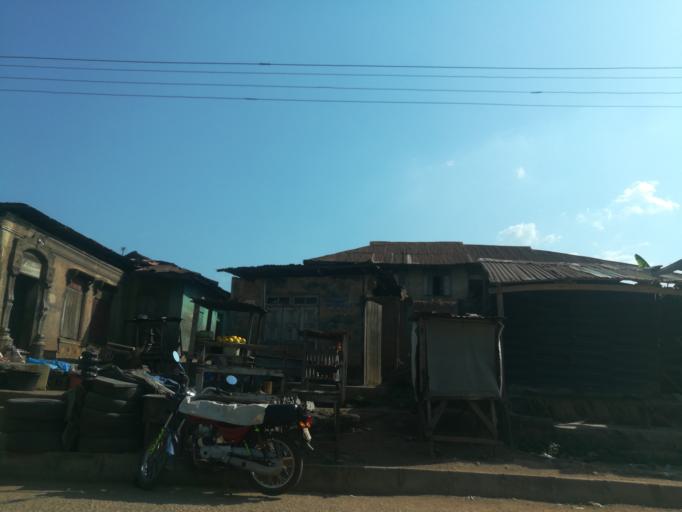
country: NG
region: Ogun
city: Abeokuta
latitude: 7.1568
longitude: 3.3375
